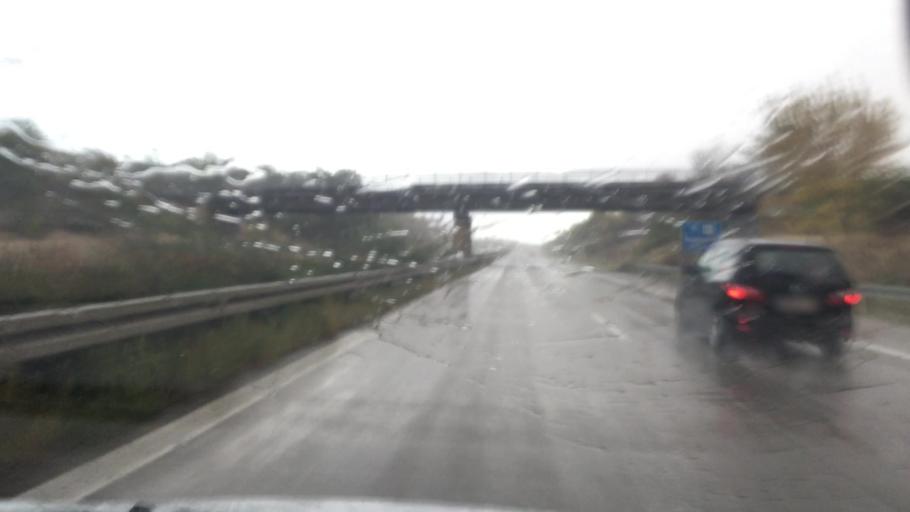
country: DE
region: Saxony-Anhalt
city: Eickendorf
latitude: 51.9499
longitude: 11.6866
